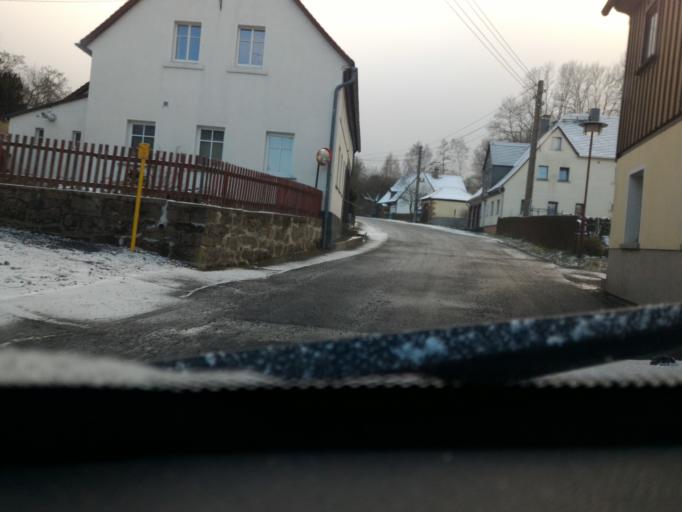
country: DE
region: Saxony
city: Grossschonau
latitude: 50.8629
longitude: 14.6503
